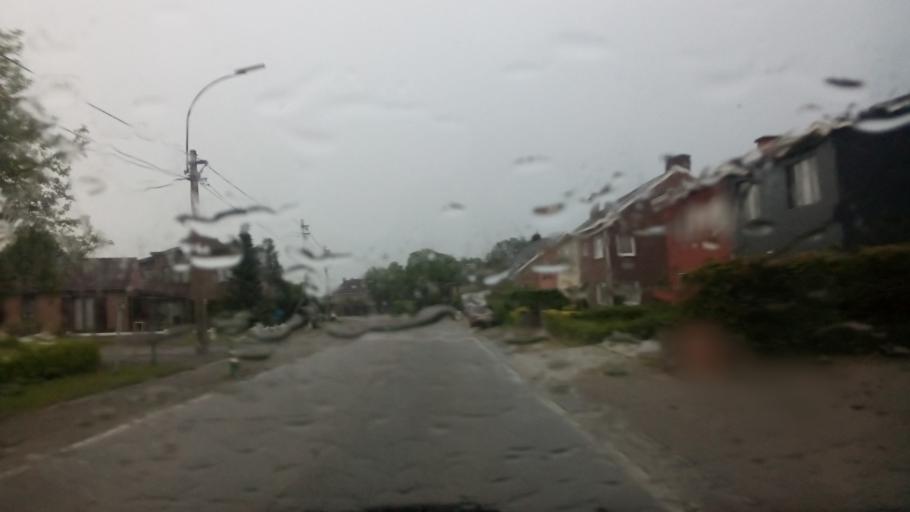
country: BE
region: Flanders
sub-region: Provincie Oost-Vlaanderen
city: Lovendegem
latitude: 51.0644
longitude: 3.6372
